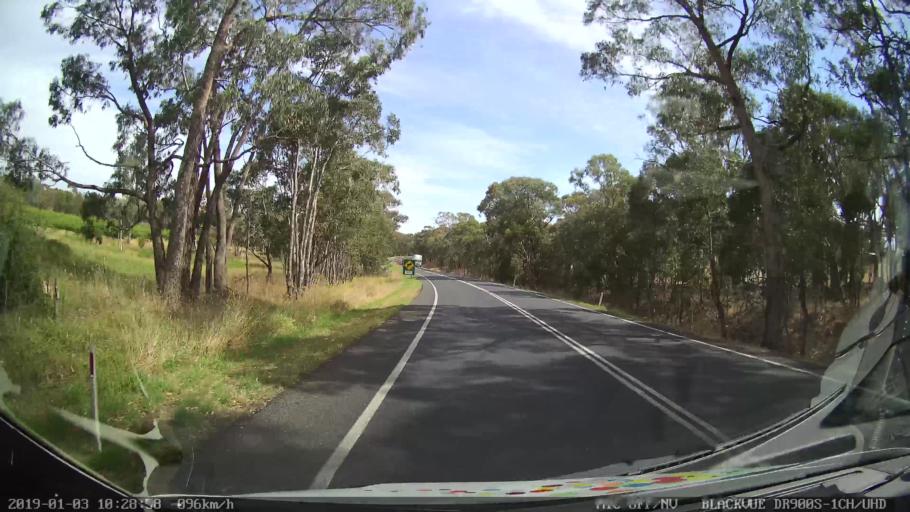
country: AU
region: New South Wales
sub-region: Young
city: Young
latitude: -34.3802
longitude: 148.2602
